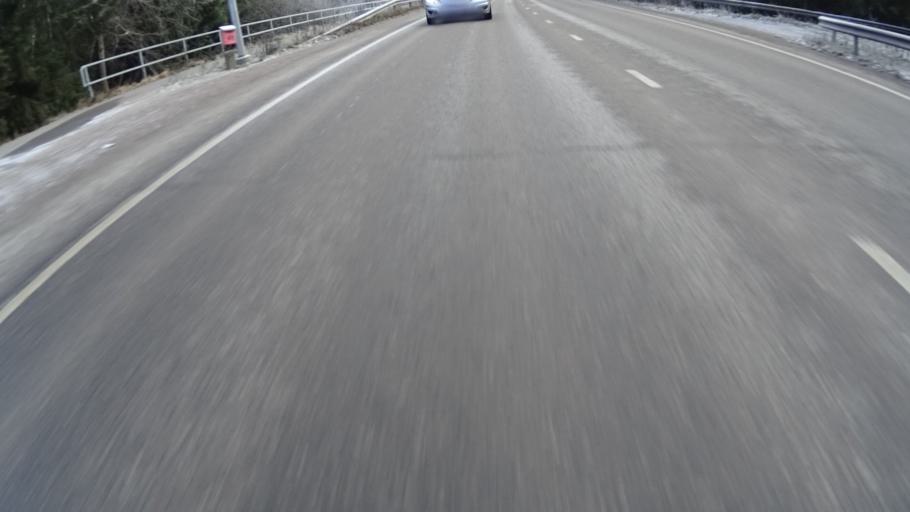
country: FI
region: Uusimaa
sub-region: Helsinki
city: Nurmijaervi
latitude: 60.3702
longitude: 24.7774
